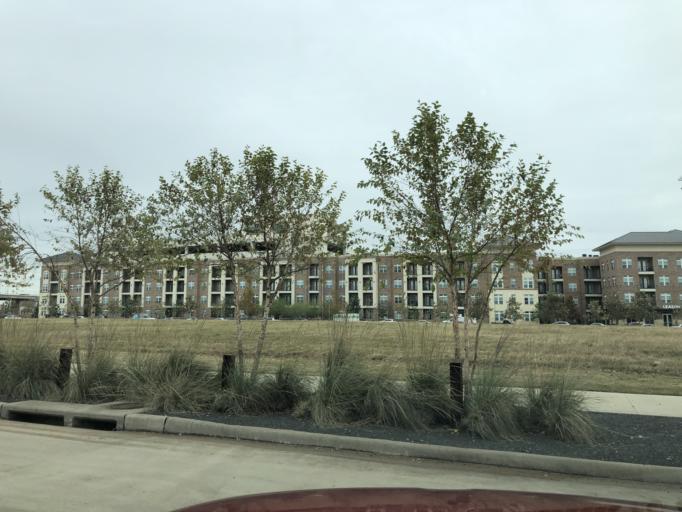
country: US
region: Texas
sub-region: Harris County
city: Houston
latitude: 29.7746
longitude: -95.3531
